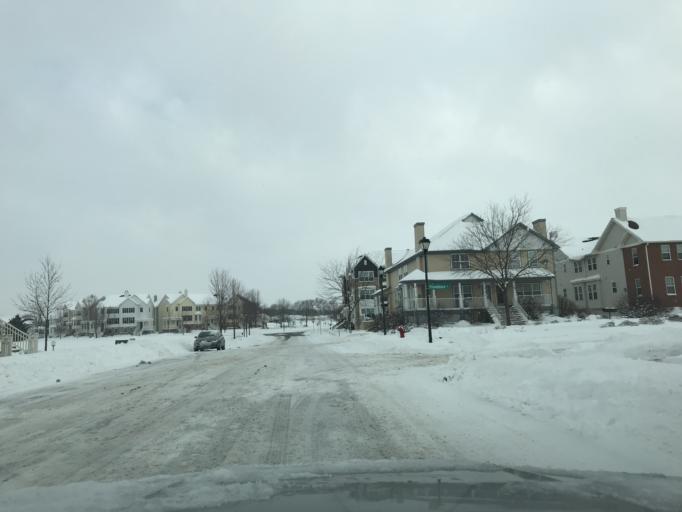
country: US
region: Wisconsin
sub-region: Dane County
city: Sun Prairie
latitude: 43.1662
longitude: -89.2778
